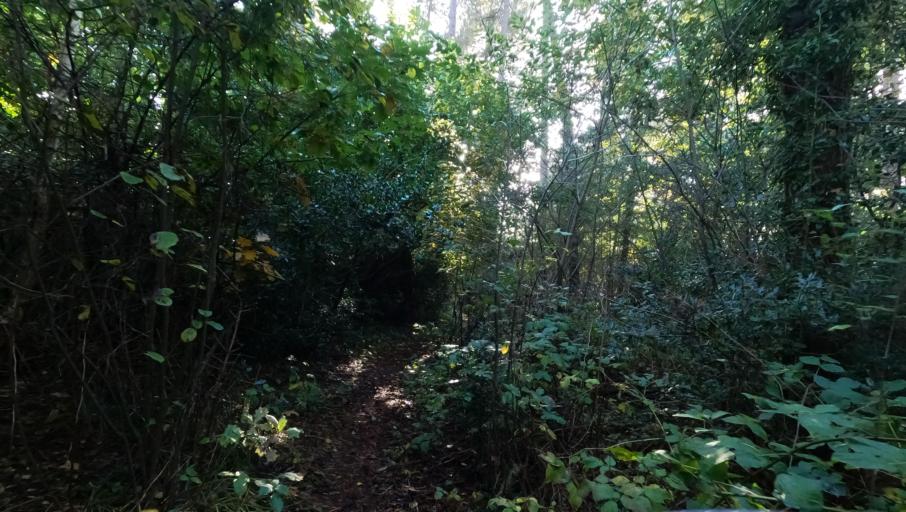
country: BE
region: Flanders
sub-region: Provincie Antwerpen
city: Schilde
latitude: 51.2477
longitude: 4.5812
